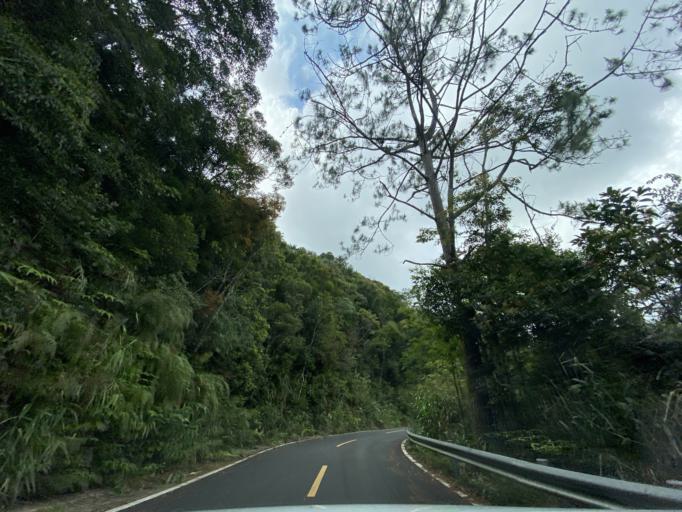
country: CN
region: Hainan
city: Diaoluoshan
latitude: 18.7082
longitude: 109.8831
